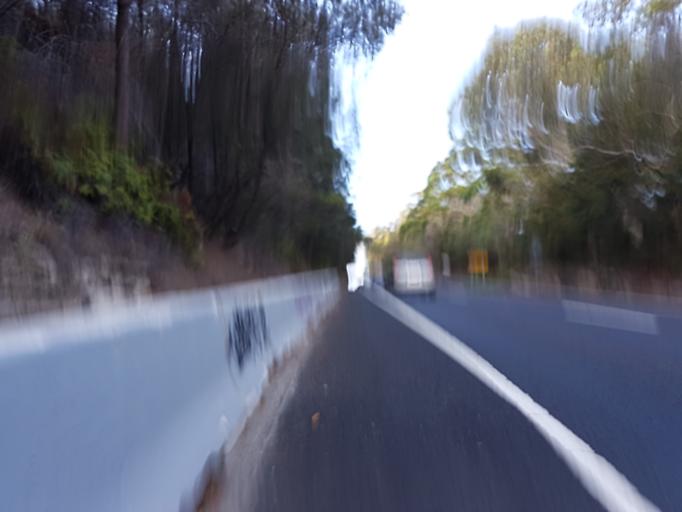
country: AU
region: New South Wales
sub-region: Warringah
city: Allambie Heights
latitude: -33.7582
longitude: 151.2331
